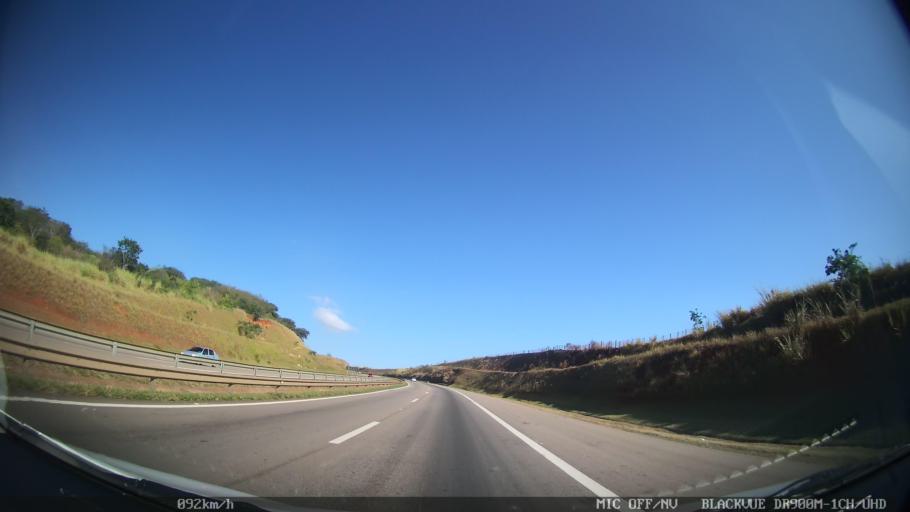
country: BR
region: Sao Paulo
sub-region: Piracicaba
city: Piracicaba
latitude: -22.7063
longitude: -47.6118
